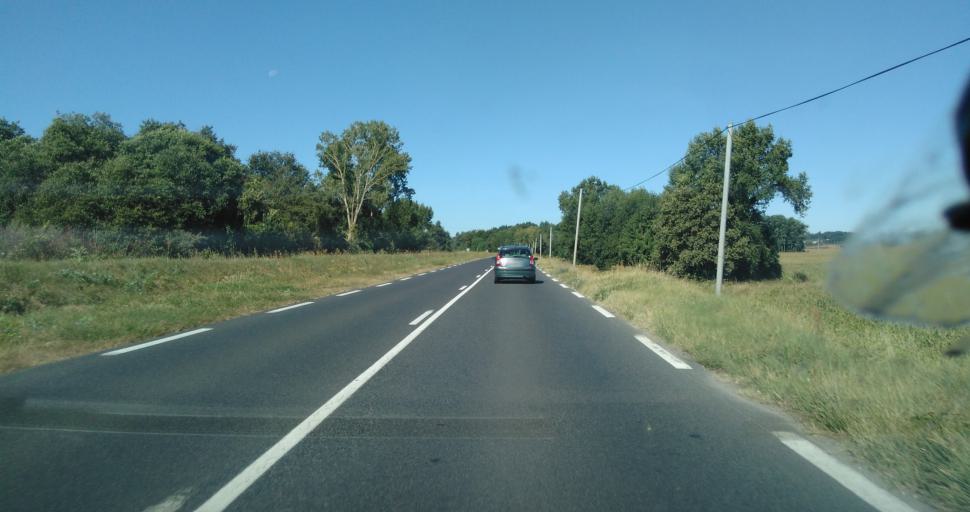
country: FR
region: Centre
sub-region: Departement d'Indre-et-Loire
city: Noizay
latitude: 47.4031
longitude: 0.9076
